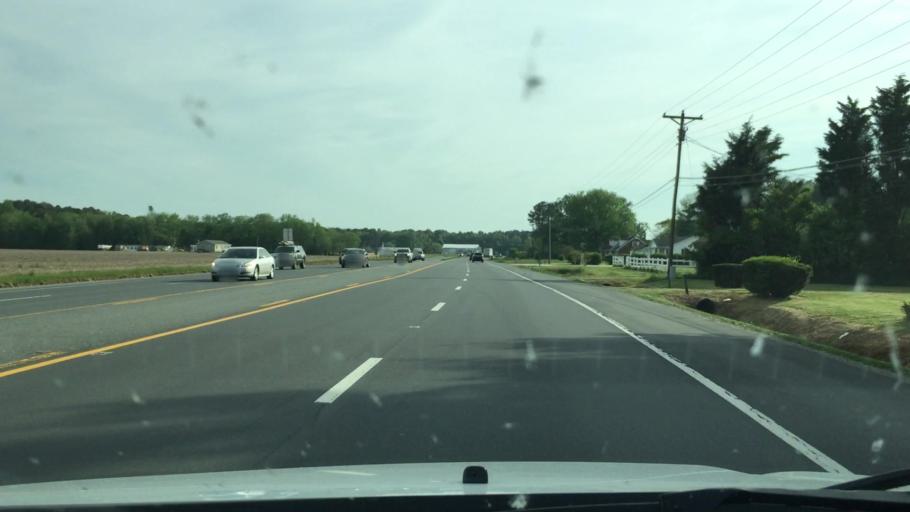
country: US
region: Virginia
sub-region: Accomack County
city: Accomac
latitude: 37.7397
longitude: -75.6441
